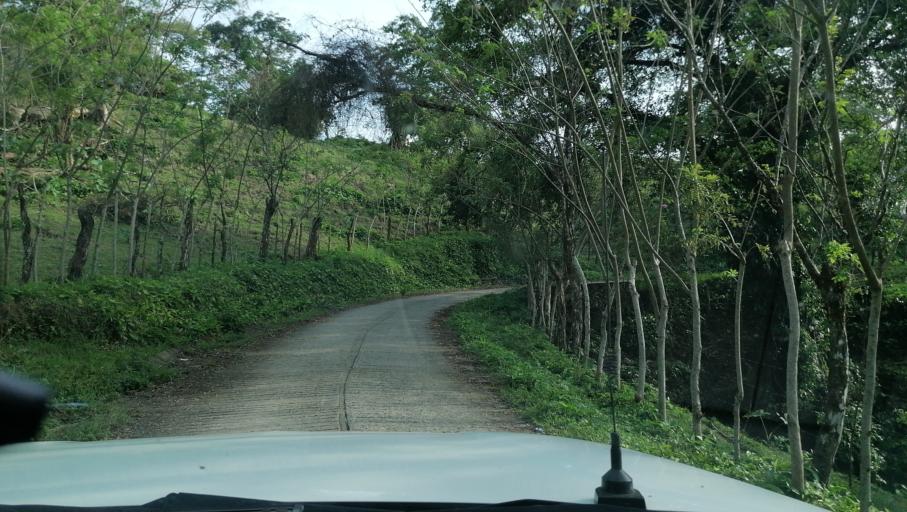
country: MX
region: Chiapas
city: Pichucalco
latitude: 17.4838
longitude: -93.2338
